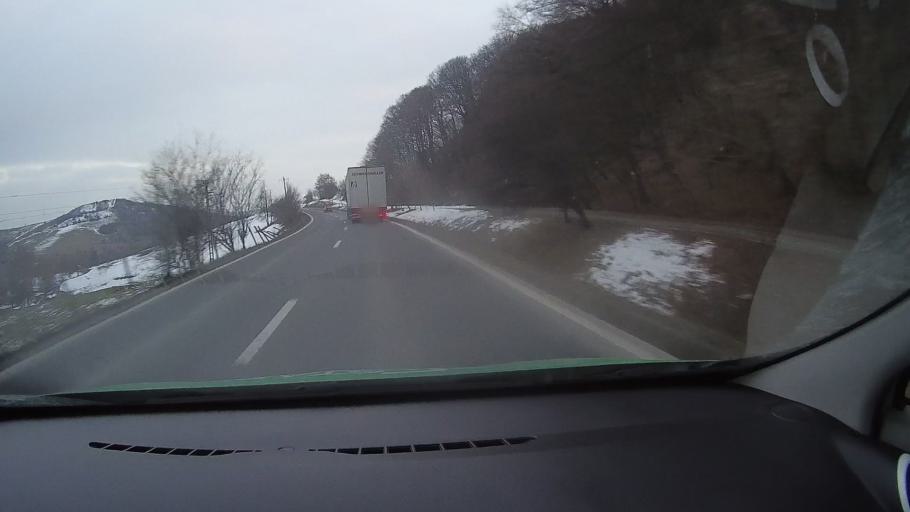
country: RO
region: Harghita
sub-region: Municipiul Odorheiu Secuiesc
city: Odorheiu Secuiesc
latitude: 46.3288
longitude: 25.2759
